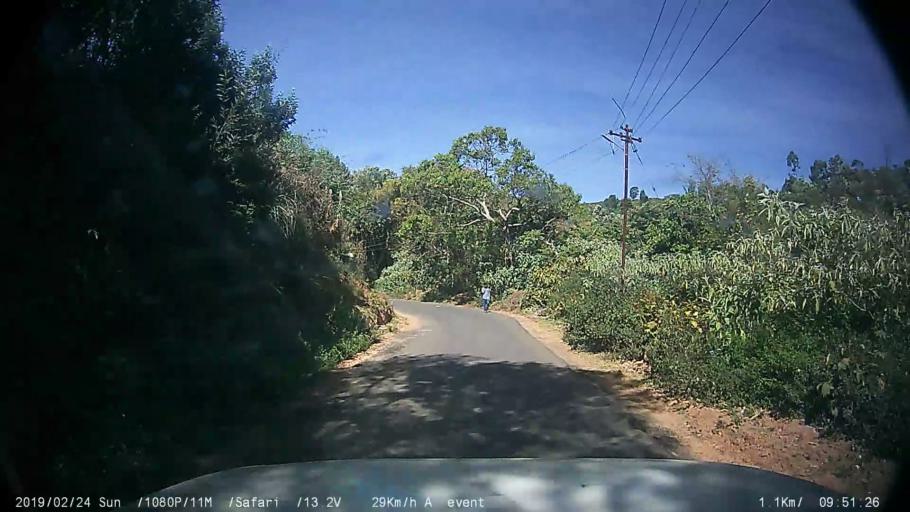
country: IN
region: Tamil Nadu
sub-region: Nilgiri
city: Wellington
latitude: 11.3518
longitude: 76.7746
